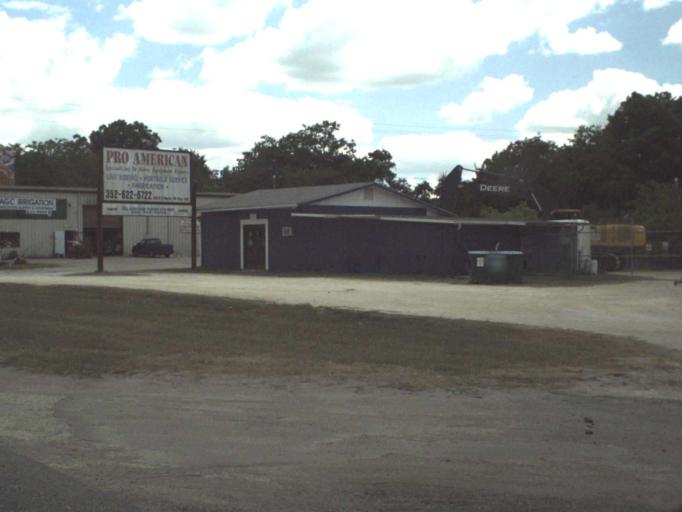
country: US
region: Florida
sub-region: Marion County
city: Ocala
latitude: 29.2387
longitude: -82.1520
